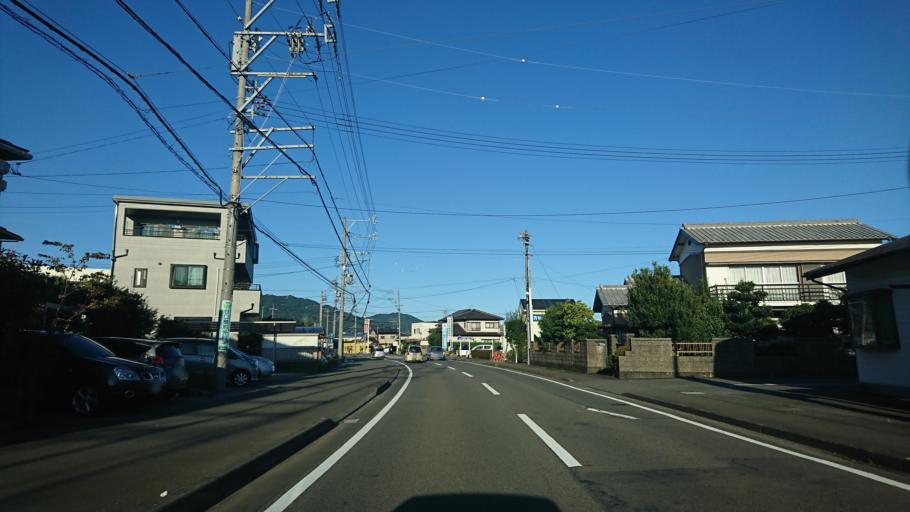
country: JP
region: Shizuoka
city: Fujieda
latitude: 34.8687
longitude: 138.2770
